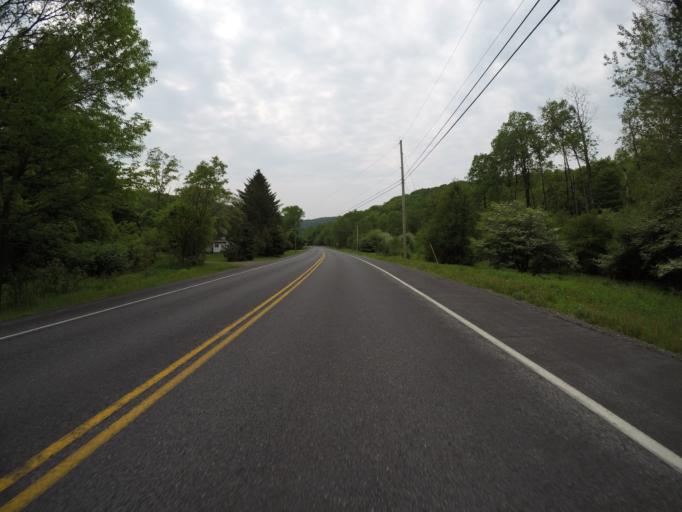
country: US
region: New York
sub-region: Sullivan County
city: Livingston Manor
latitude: 41.9847
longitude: -74.8948
